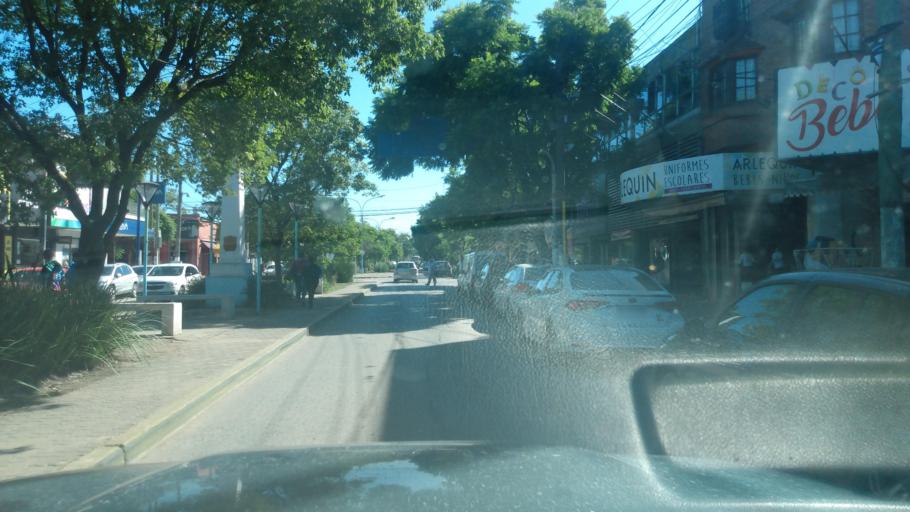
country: AR
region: Buenos Aires
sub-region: Partido de General Rodriguez
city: General Rodriguez
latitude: -34.6087
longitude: -58.9513
